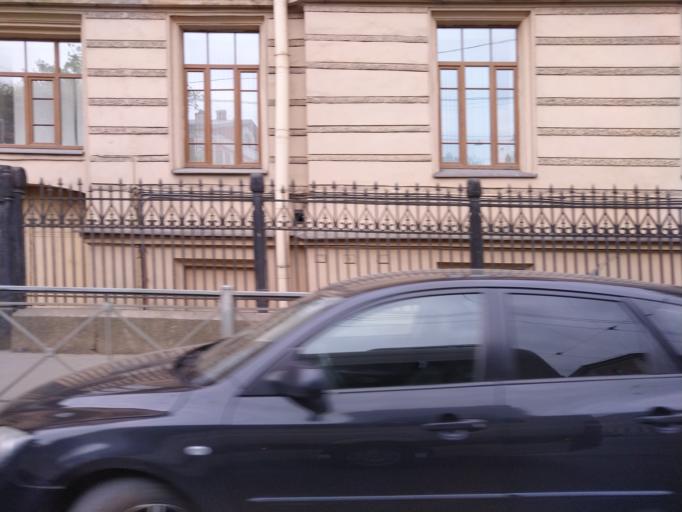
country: RU
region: Leningrad
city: Finlyandskiy
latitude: 59.9552
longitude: 30.3688
